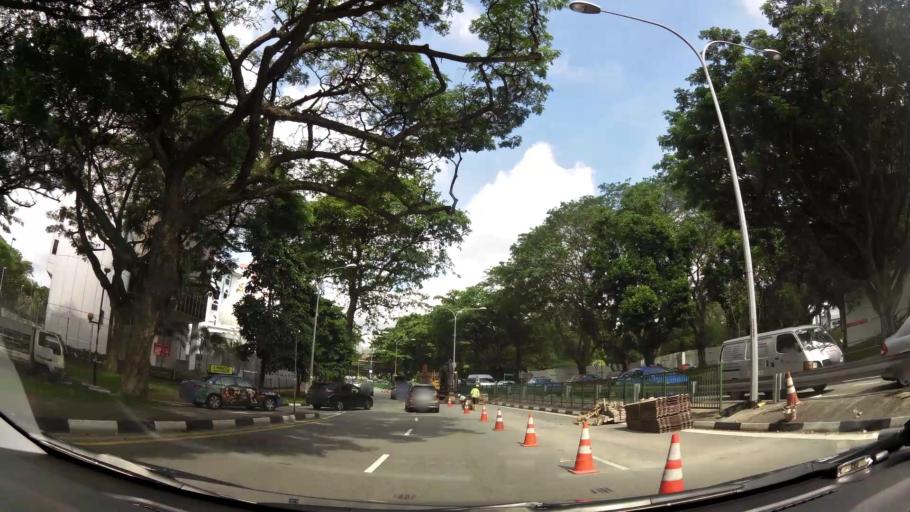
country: SG
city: Singapore
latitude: 1.2768
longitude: 103.8333
